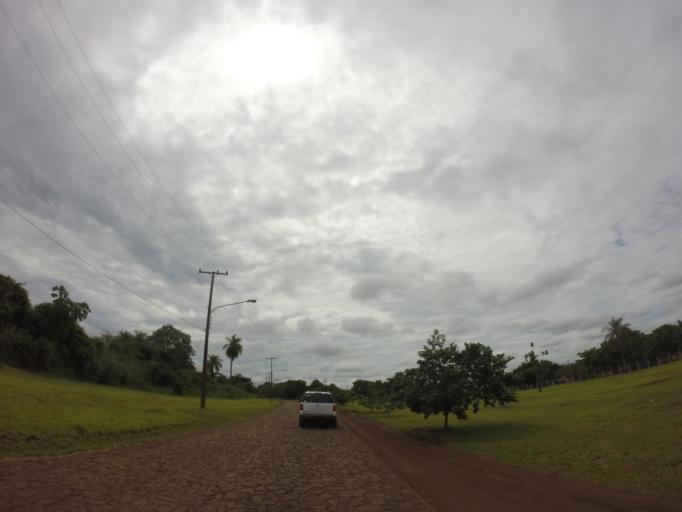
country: PY
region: Alto Parana
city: Ciudad del Este
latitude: -25.3905
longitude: -54.6253
